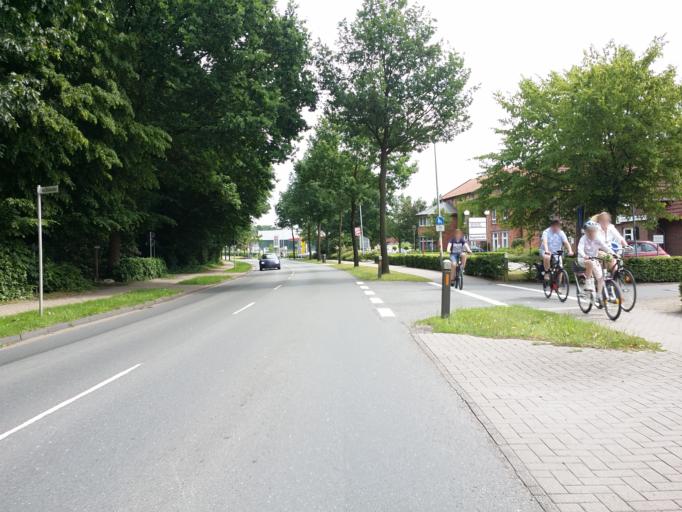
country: DE
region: Lower Saxony
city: Wiefelstede
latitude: 53.2517
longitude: 8.1185
